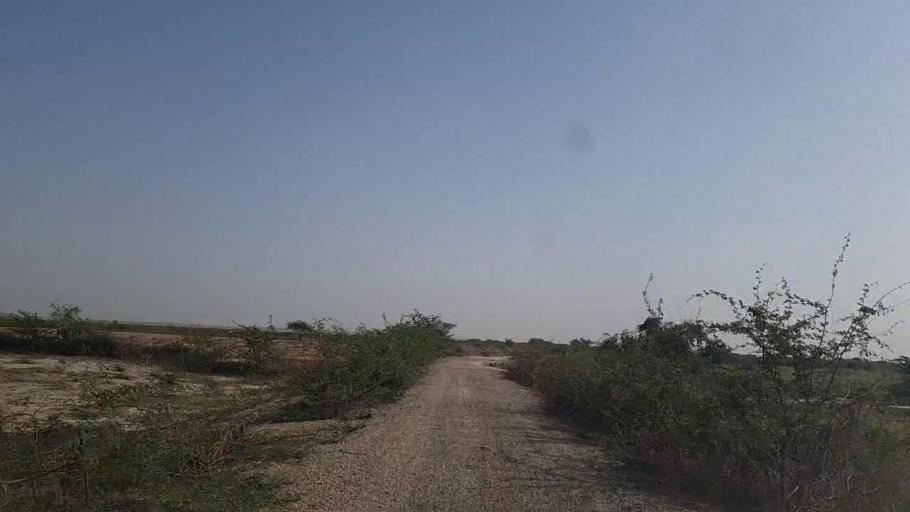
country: PK
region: Sindh
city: Kadhan
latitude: 24.5870
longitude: 69.2628
